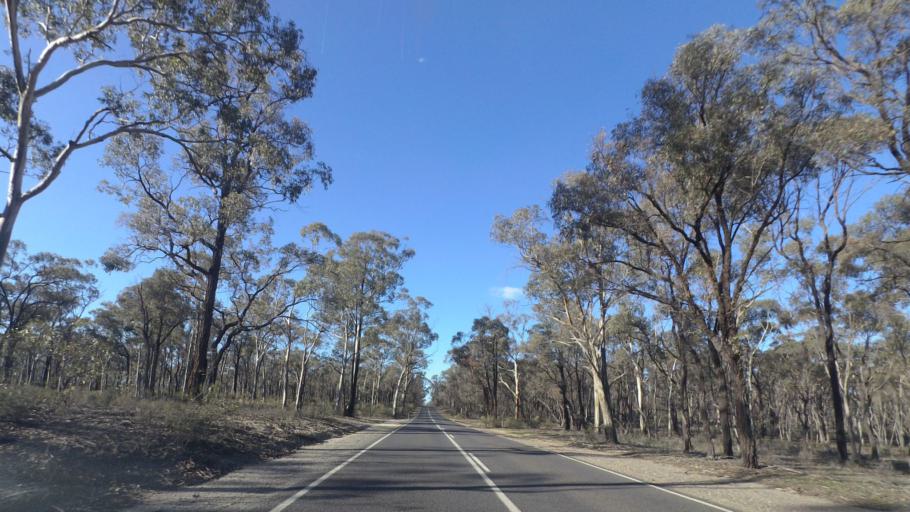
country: AU
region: Victoria
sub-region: Greater Bendigo
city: Epsom
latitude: -36.6656
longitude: 144.4388
